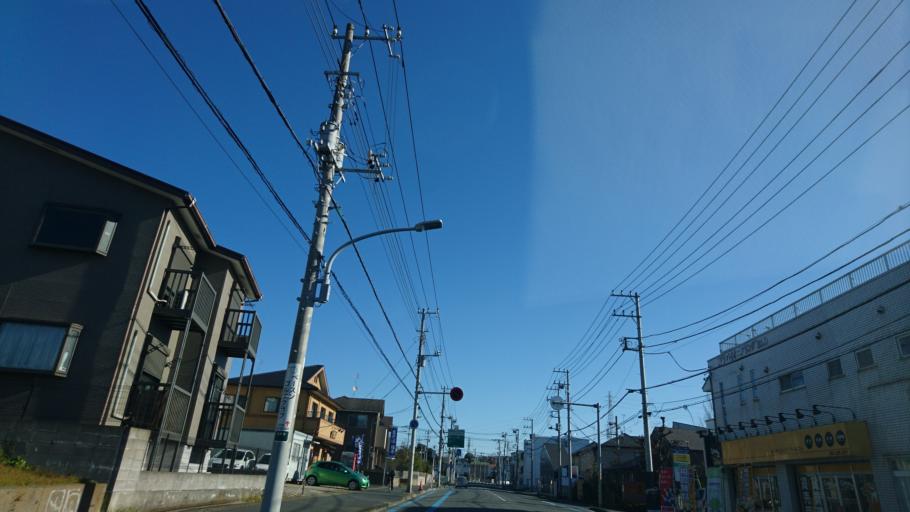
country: JP
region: Chiba
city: Chiba
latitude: 35.5840
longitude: 140.1406
